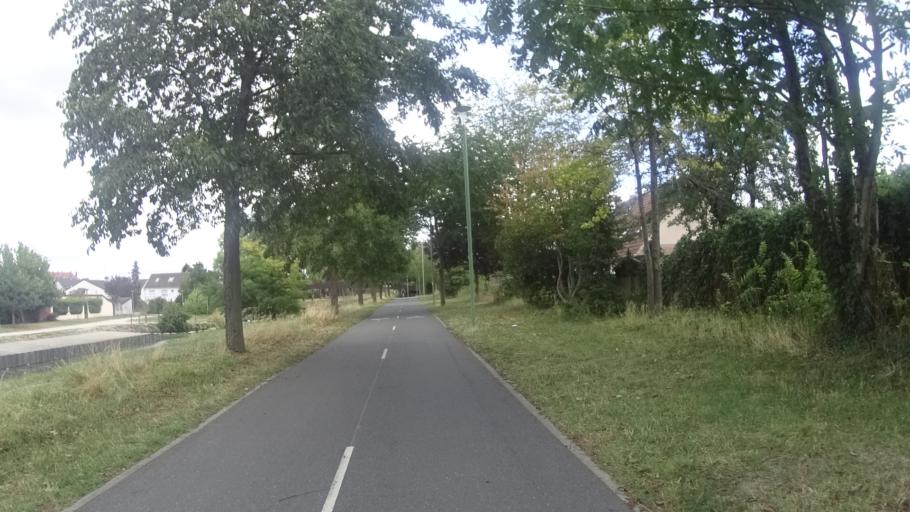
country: FR
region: Ile-de-France
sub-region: Departement de Seine-Saint-Denis
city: Les Pavillons-sous-Bois
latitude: 48.9194
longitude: 2.5078
